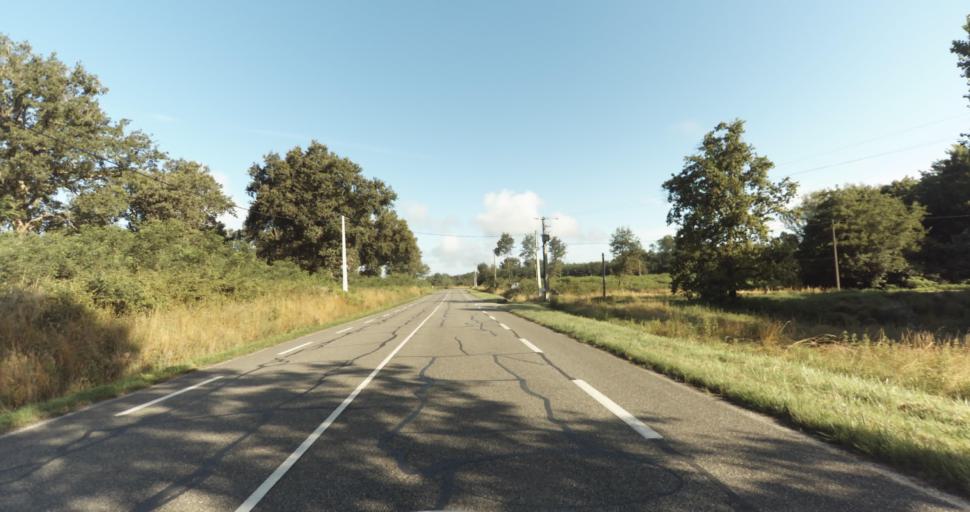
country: FR
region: Aquitaine
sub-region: Departement de la Gironde
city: Bazas
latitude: 44.4513
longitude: -0.2468
